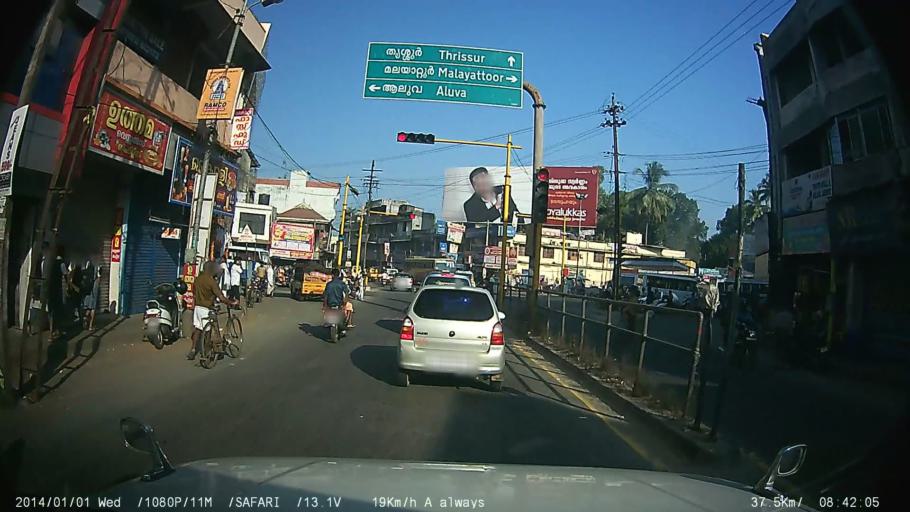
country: IN
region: Kerala
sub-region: Ernakulam
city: Angamali
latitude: 10.1657
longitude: 76.4391
